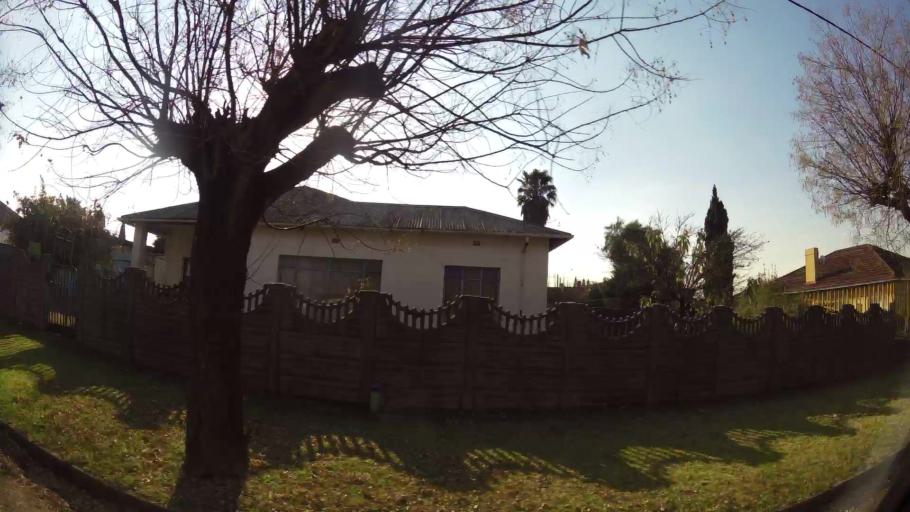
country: ZA
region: Gauteng
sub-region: Ekurhuleni Metropolitan Municipality
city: Brakpan
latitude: -26.2319
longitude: 28.3589
